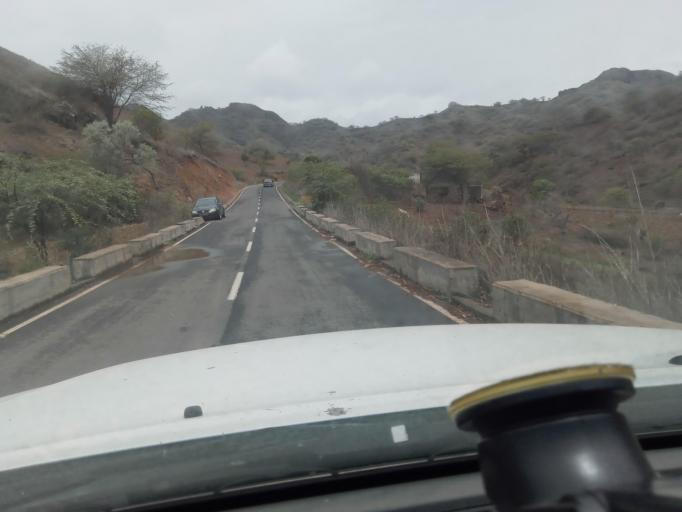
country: CV
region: Sao Miguel
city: Calheta
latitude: 15.1450
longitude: -23.6162
